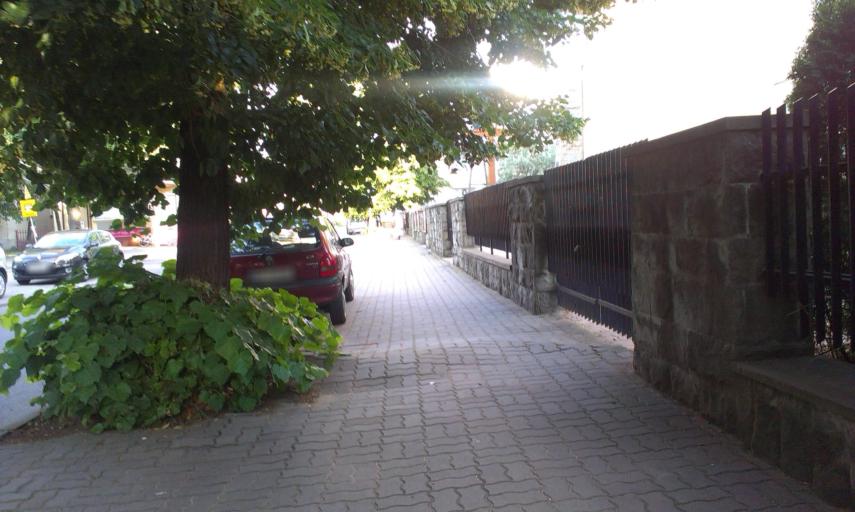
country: PL
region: Masovian Voivodeship
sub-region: Warszawa
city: Ursus
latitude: 52.1941
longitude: 20.8856
